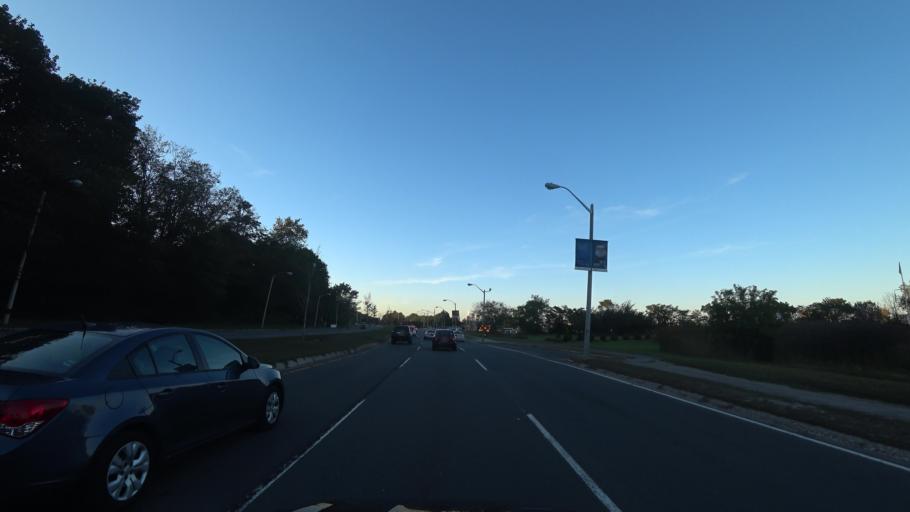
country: US
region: Massachusetts
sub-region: Suffolk County
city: South Boston
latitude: 42.3107
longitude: -71.0454
